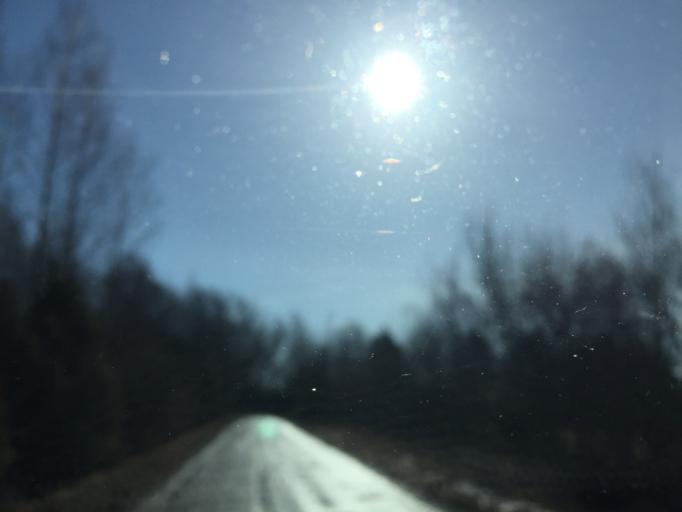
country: EE
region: Laeaene
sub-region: Haapsalu linn
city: Haapsalu
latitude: 58.6839
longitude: 23.5116
